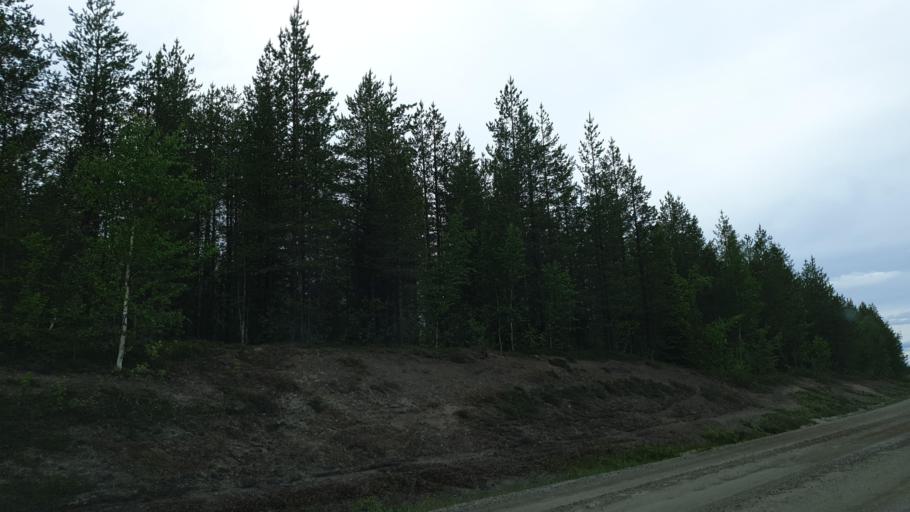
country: SE
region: Vaesterbotten
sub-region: Sorsele Kommun
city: Sorsele
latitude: 65.5557
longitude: 17.5055
